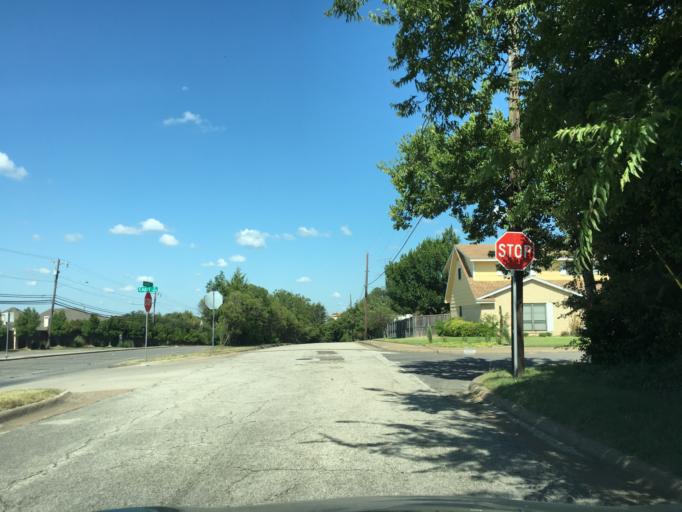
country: US
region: Texas
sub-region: Dallas County
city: Garland
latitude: 32.8644
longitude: -96.6945
